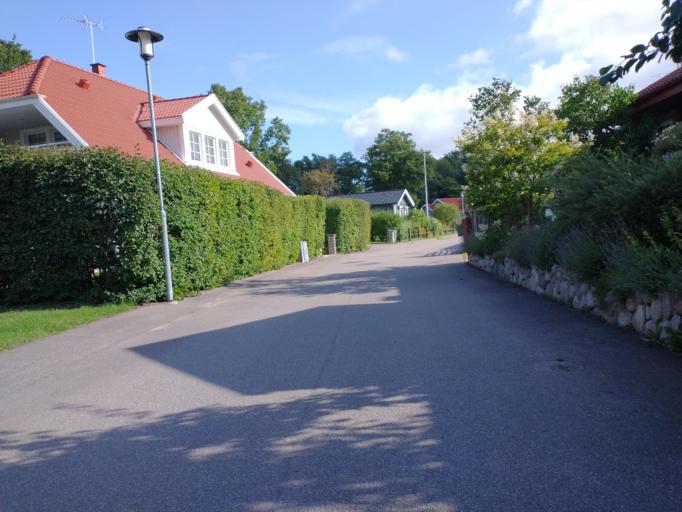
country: SE
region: Kalmar
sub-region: Kalmar Kommun
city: Lindsdal
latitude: 56.7805
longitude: 16.3034
